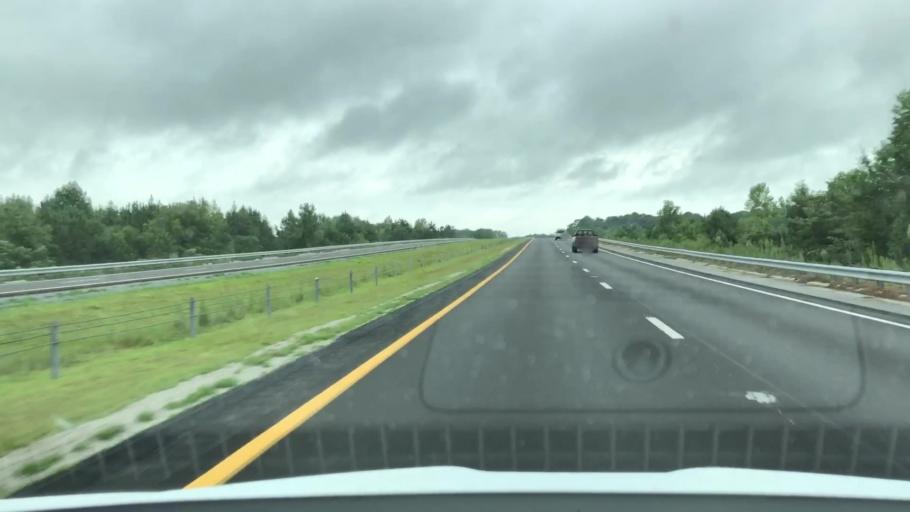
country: US
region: North Carolina
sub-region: Wayne County
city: Fremont
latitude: 35.4656
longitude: -77.9861
